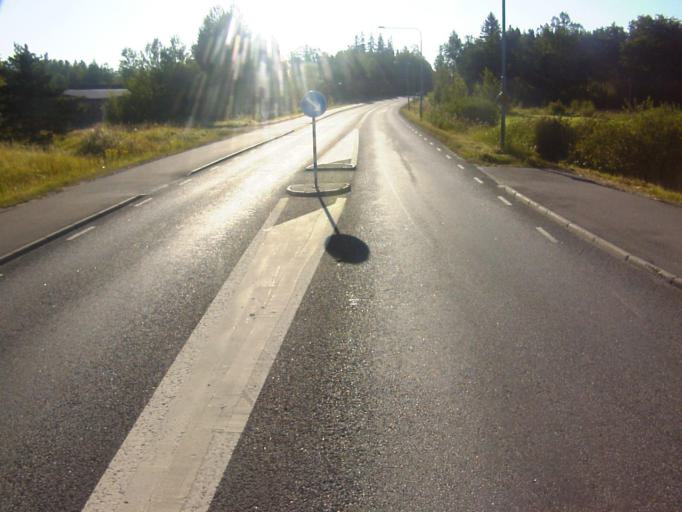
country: SE
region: Soedermanland
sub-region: Eskilstuna Kommun
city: Hallbybrunn
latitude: 59.3976
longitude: 16.4347
